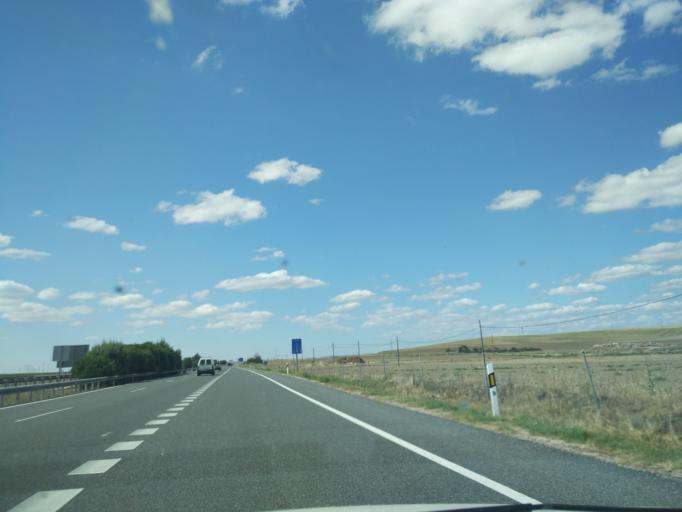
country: ES
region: Castille and Leon
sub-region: Provincia de Valladolid
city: Ataquines
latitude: 41.1835
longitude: -4.8086
